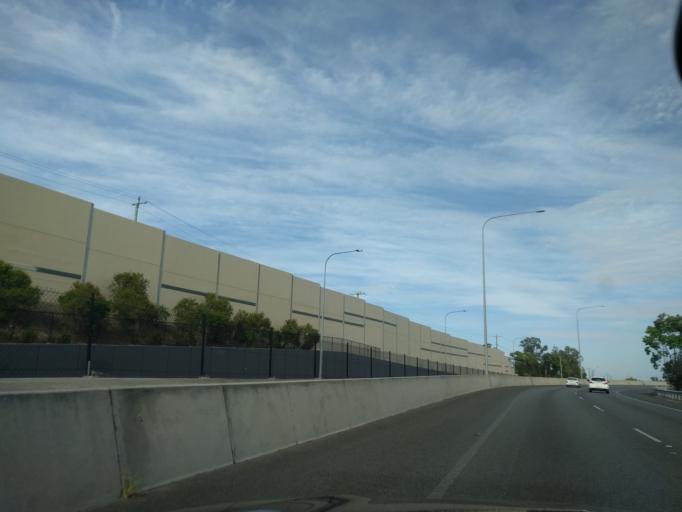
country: AU
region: Queensland
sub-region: Ipswich
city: Riverview
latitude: -27.5968
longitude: 152.8433
